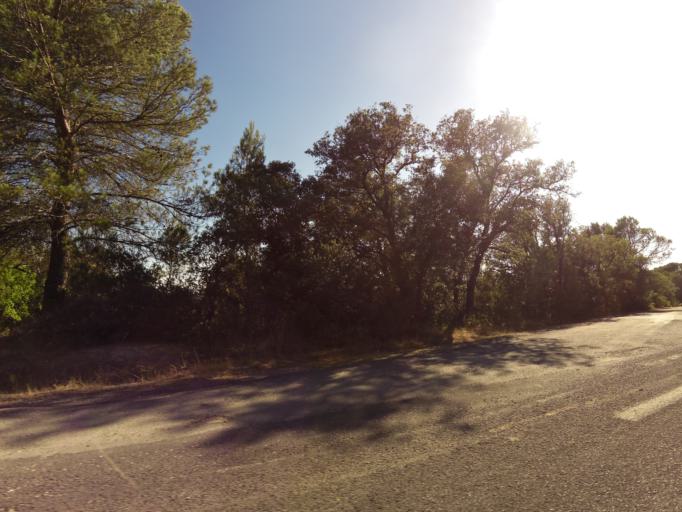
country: FR
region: Languedoc-Roussillon
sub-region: Departement de l'Herault
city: Boisseron
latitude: 43.7601
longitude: 4.1068
